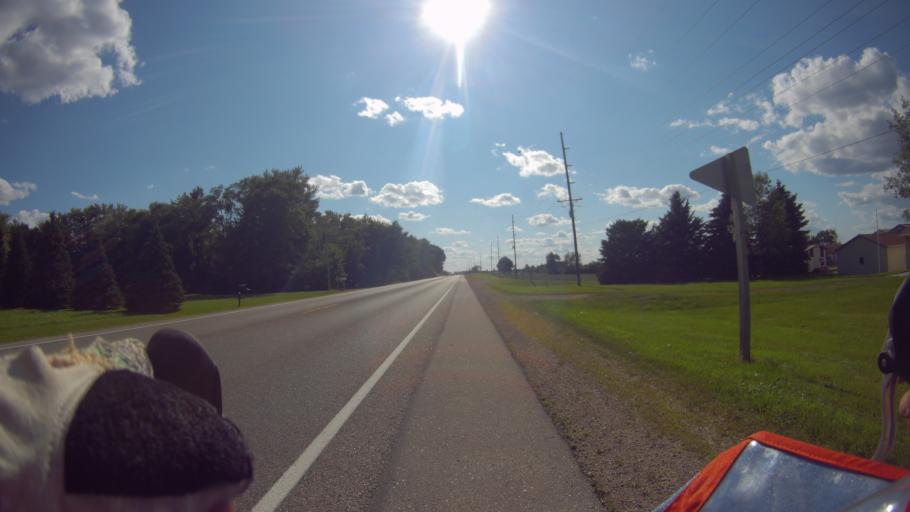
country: US
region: Wisconsin
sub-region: Dane County
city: Oregon
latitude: 42.9188
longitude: -89.3365
